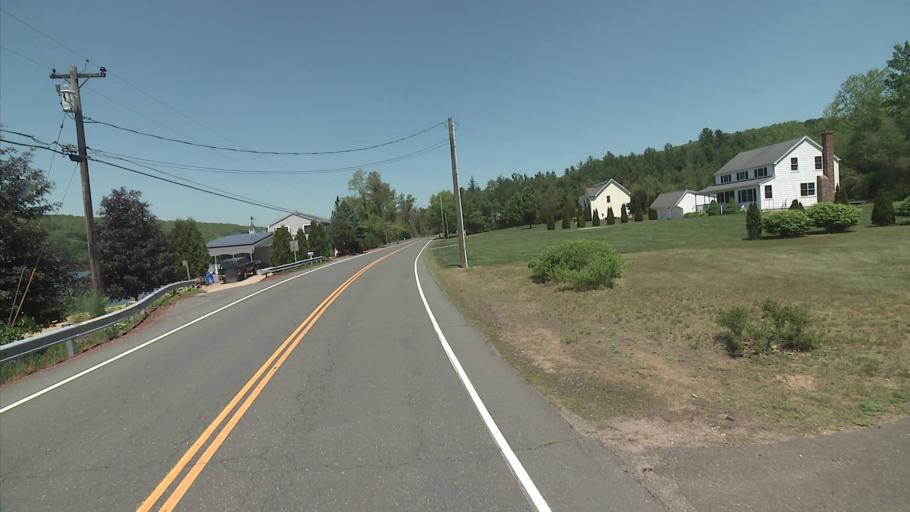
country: US
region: Connecticut
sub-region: Tolland County
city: Stafford
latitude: 41.9968
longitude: -72.2554
